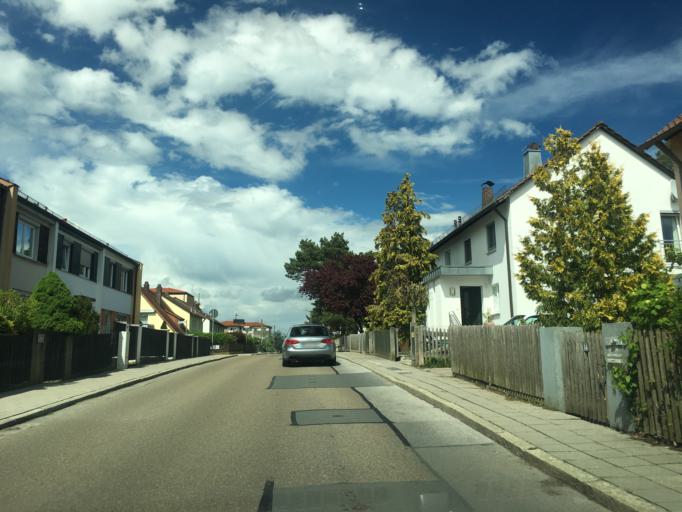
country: DE
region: Bavaria
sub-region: Upper Palatinate
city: Neumarkt in der Oberpfalz
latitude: 49.2792
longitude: 11.4775
